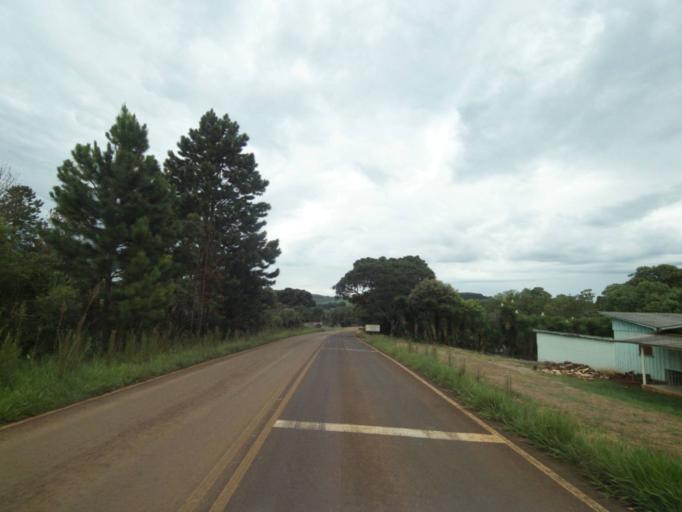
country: BR
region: Parana
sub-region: Pitanga
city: Pitanga
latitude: -24.8949
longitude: -51.9611
